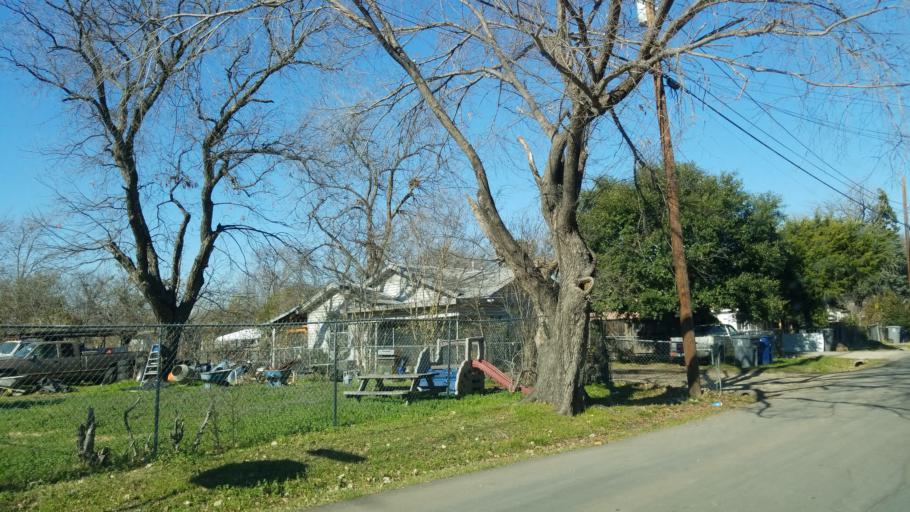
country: US
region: Texas
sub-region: Dallas County
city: Cockrell Hill
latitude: 32.7527
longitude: -96.9140
